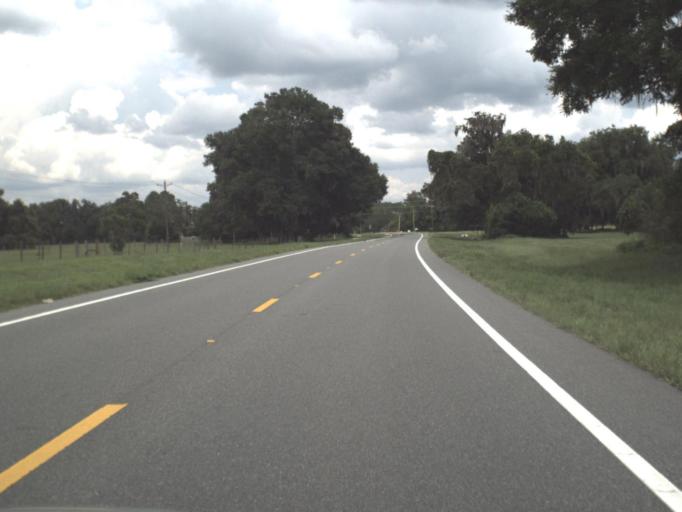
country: US
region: Florida
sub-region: Alachua County
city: Alachua
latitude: 29.8143
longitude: -82.4611
